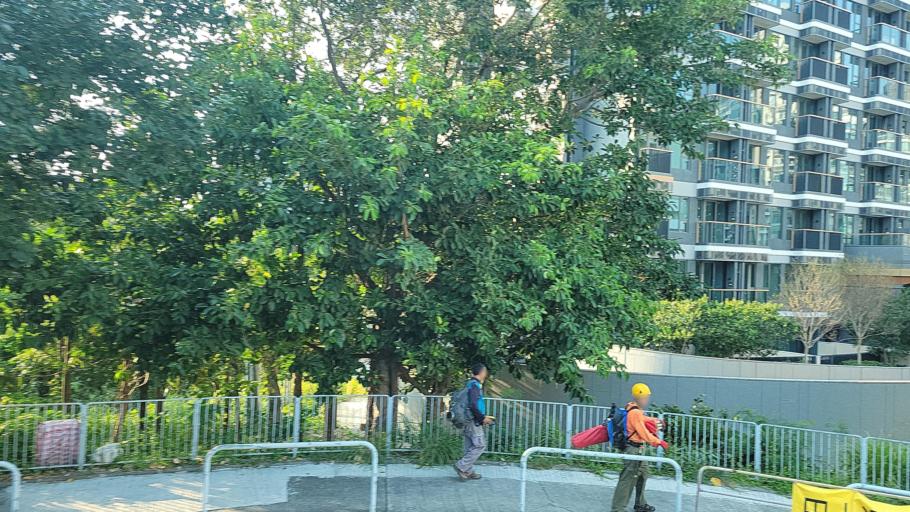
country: HK
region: Tuen Mun
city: Tuen Mun
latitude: 22.3714
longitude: 114.0035
